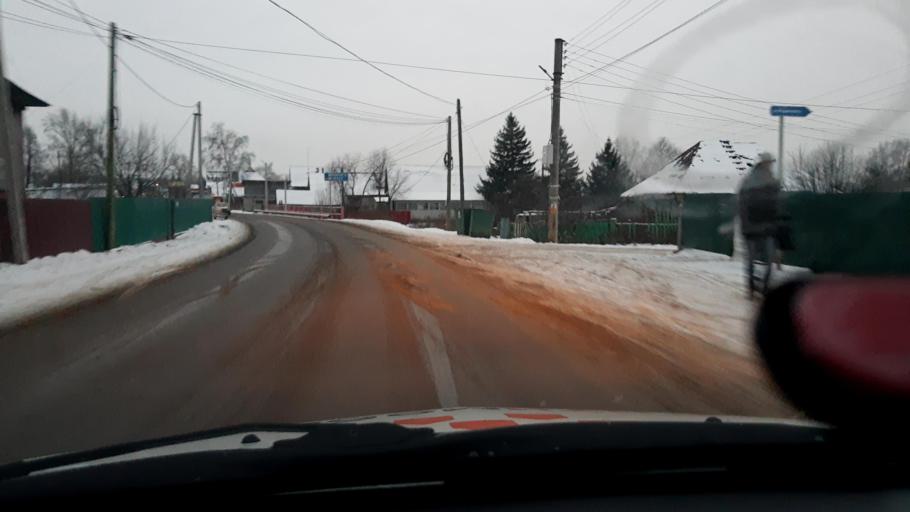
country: RU
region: Bashkortostan
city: Iglino
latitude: 54.8476
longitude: 56.4442
